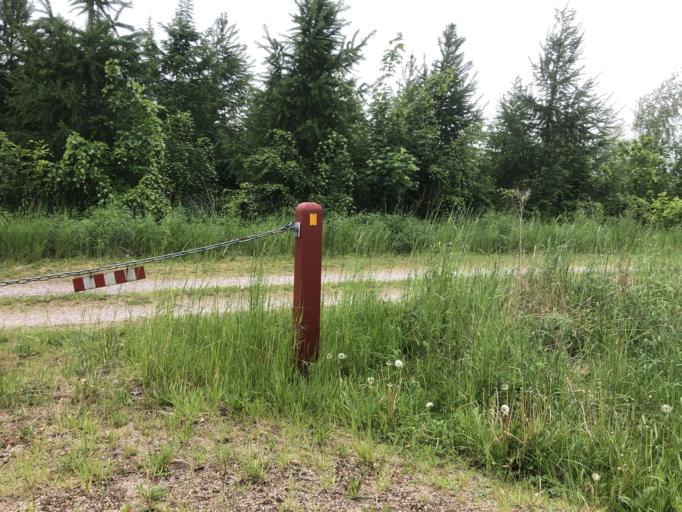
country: DK
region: South Denmark
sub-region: Odense Kommune
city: Bellinge
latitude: 55.3720
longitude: 10.3074
